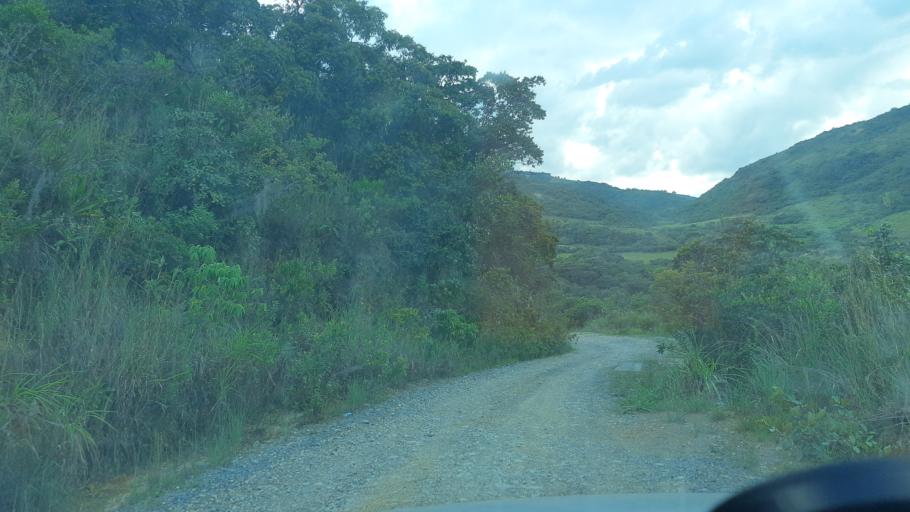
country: CO
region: Boyaca
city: Santa Sofia
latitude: 5.7458
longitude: -73.5773
